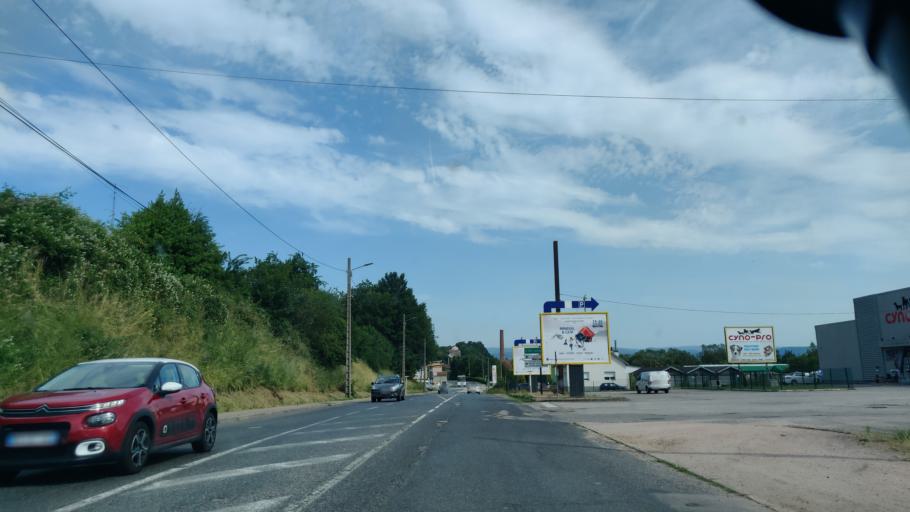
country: FR
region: Lorraine
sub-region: Departement des Vosges
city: Saint-Die-des-Vosges
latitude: 48.2961
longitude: 6.9363
